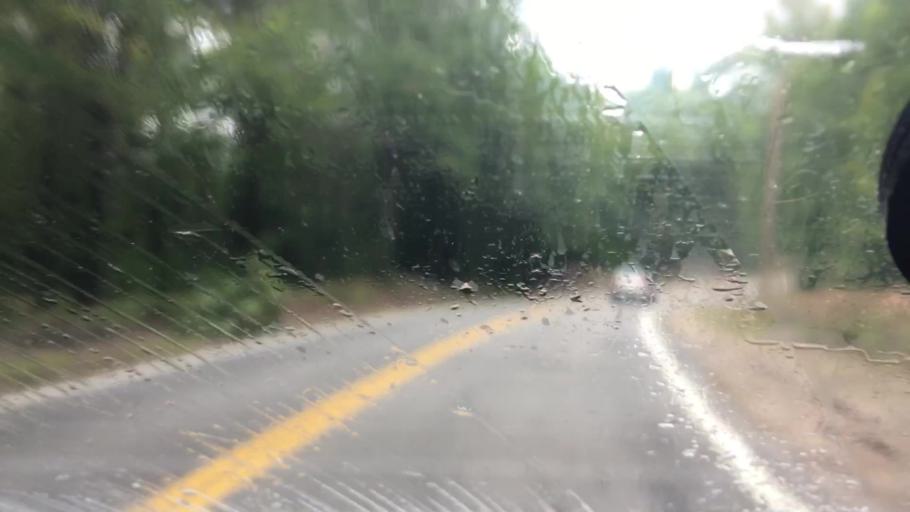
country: US
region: Maine
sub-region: York County
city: Parsonsfield
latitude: 43.6737
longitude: -70.9911
